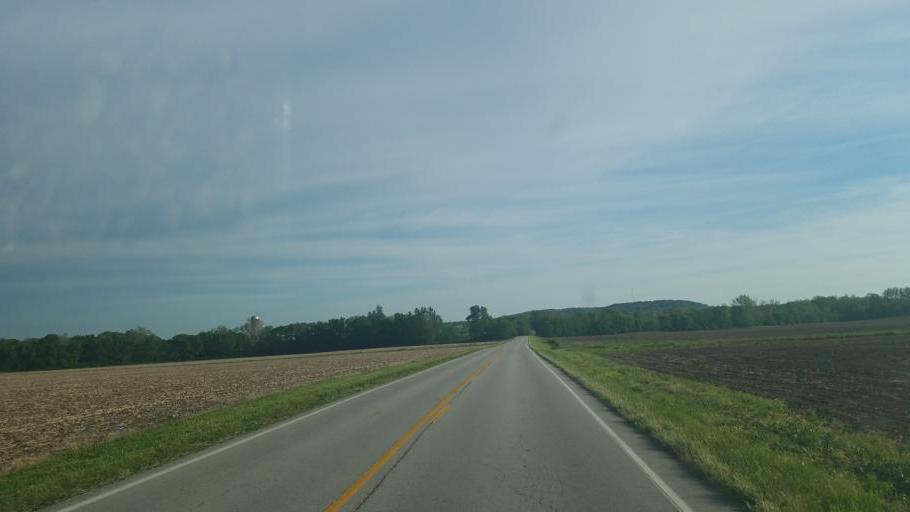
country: US
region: Ohio
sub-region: Ross County
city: Frankfort
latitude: 39.4347
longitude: -83.2243
